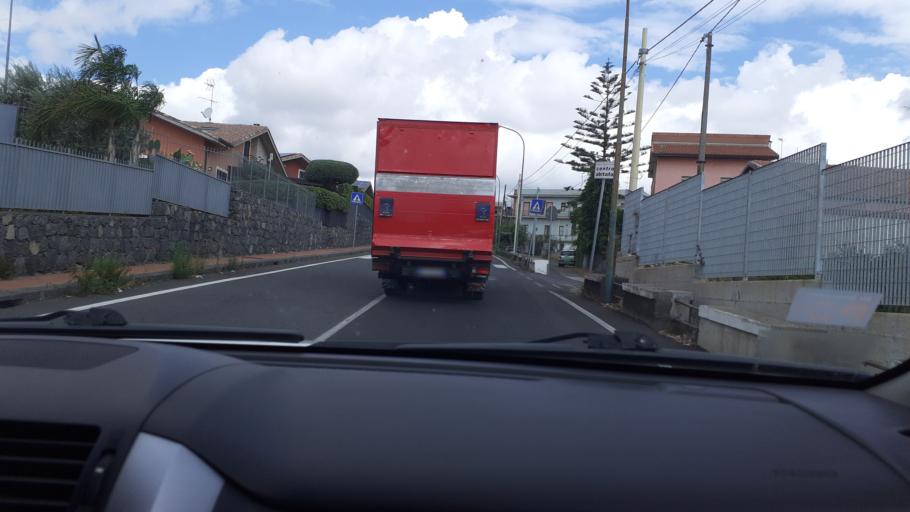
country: IT
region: Sicily
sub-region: Catania
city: Cerza
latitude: 37.5482
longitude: 15.1003
